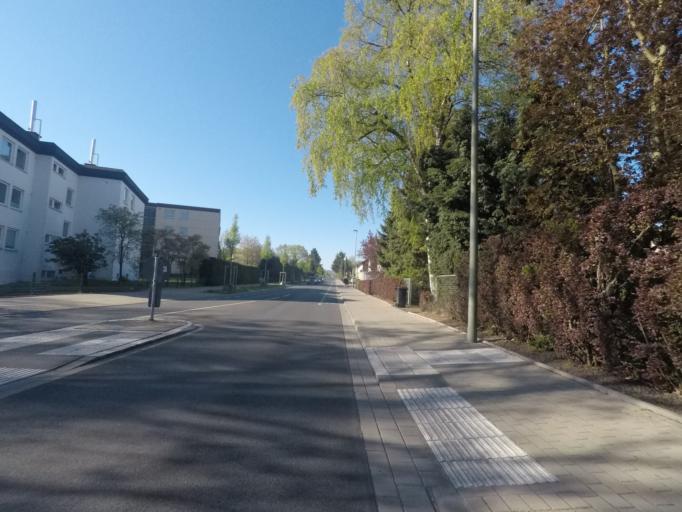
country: DE
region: North Rhine-Westphalia
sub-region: Regierungsbezirk Detmold
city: Bielefeld
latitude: 52.0265
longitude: 8.6026
